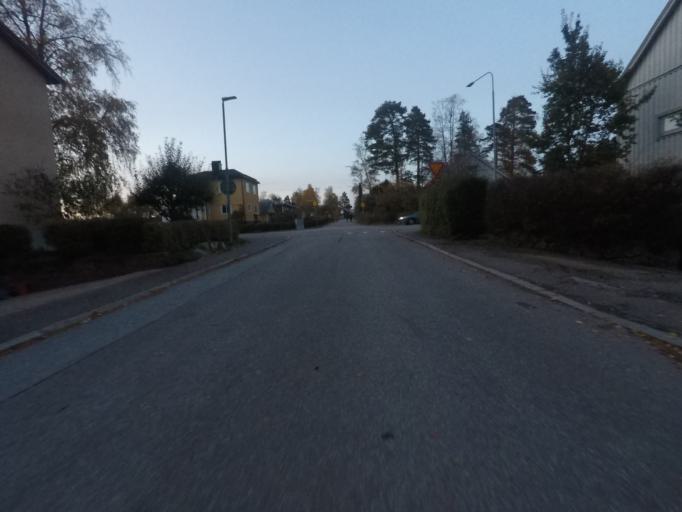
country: SE
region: OErebro
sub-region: Karlskoga Kommun
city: Karlskoga
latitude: 59.3089
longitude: 14.5027
